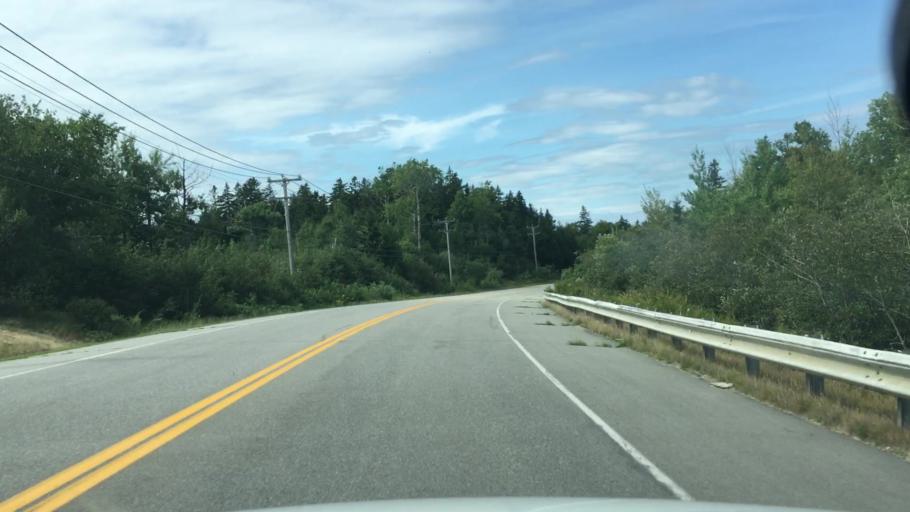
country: US
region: Maine
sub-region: Washington County
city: Eastport
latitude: 44.9281
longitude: -67.0253
